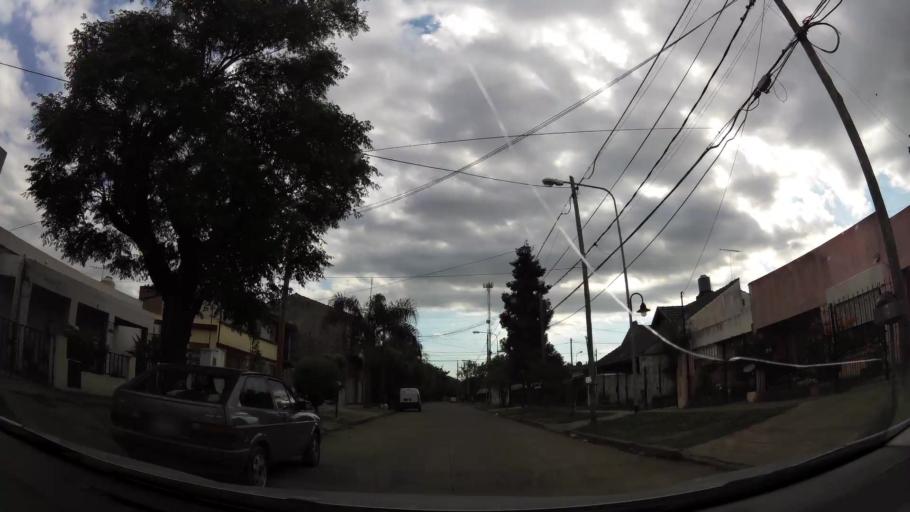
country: AR
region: Buenos Aires
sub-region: Partido de Tigre
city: Tigre
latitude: -34.4673
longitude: -58.6502
